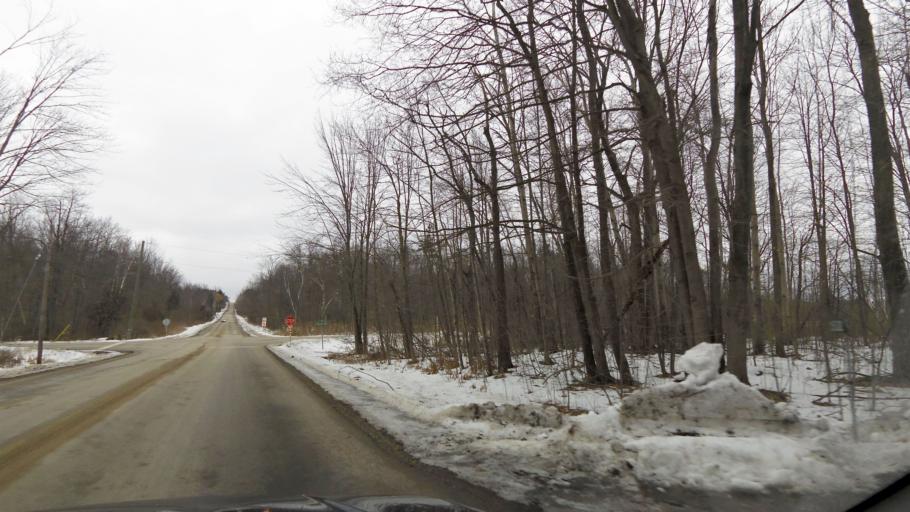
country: CA
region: Ontario
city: Brampton
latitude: 43.8693
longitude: -79.8189
